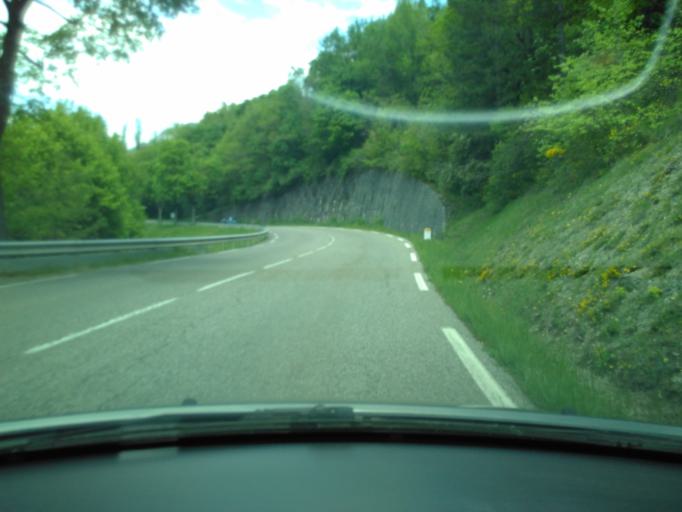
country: FR
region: Rhone-Alpes
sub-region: Departement de la Drome
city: Die
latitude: 44.6083
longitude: 5.4537
